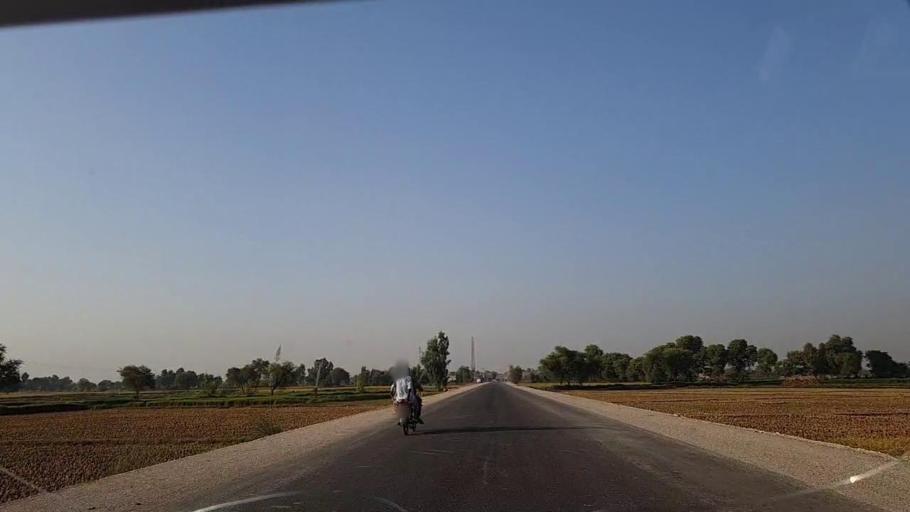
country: PK
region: Sindh
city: Rustam jo Goth
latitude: 27.9571
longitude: 68.8075
